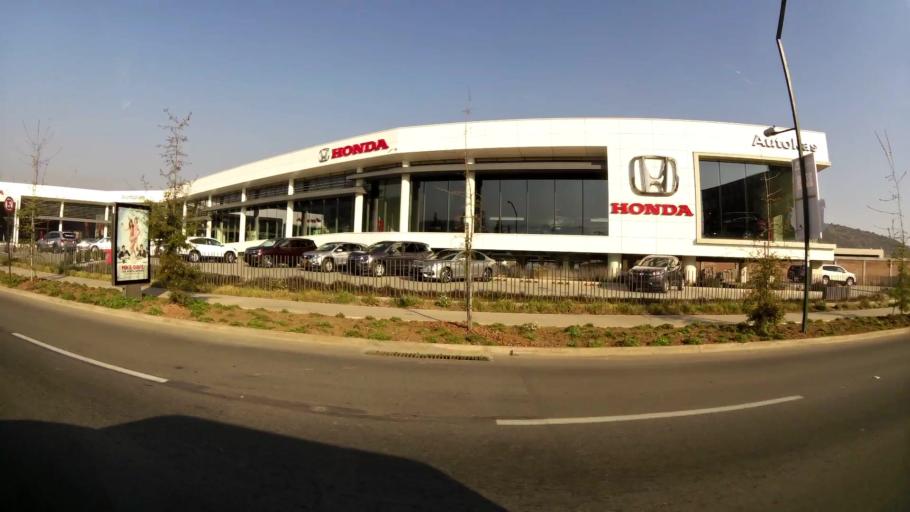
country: CL
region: Santiago Metropolitan
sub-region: Provincia de Santiago
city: Villa Presidente Frei, Nunoa, Santiago, Chile
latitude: -33.3568
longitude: -70.5387
